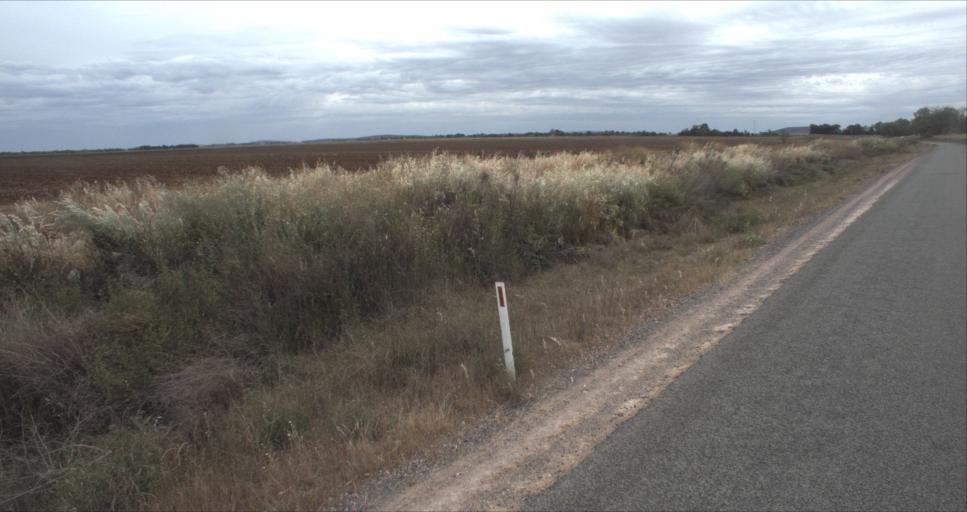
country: AU
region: New South Wales
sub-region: Leeton
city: Leeton
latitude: -34.4310
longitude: 146.3774
